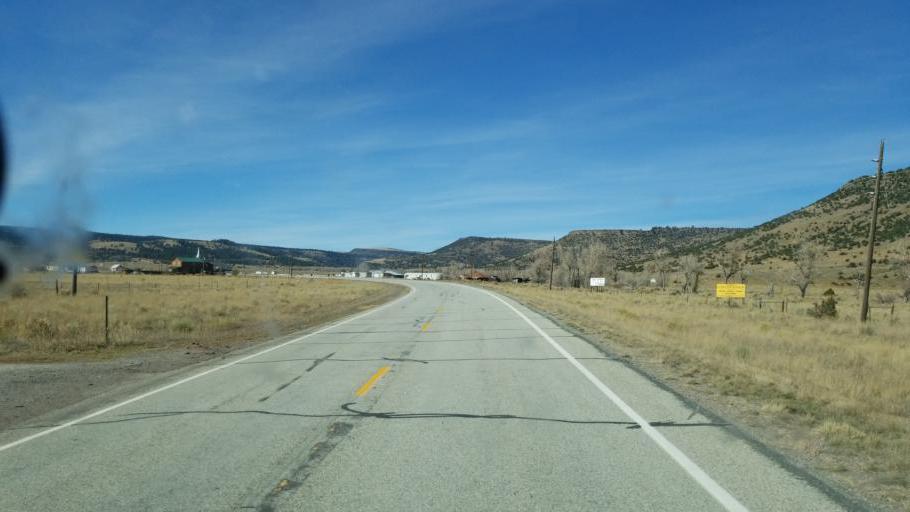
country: US
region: Colorado
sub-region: Conejos County
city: Conejos
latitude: 37.0640
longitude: -106.1951
